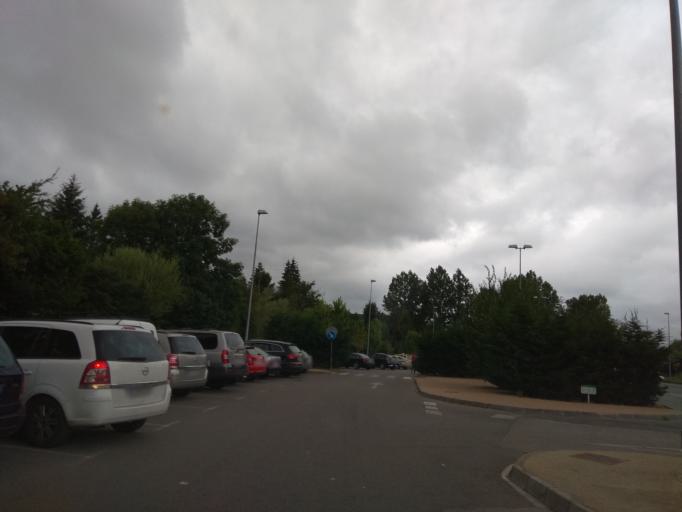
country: ES
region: Cantabria
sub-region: Provincia de Cantabria
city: Reinosa
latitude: 42.9994
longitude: -4.1394
